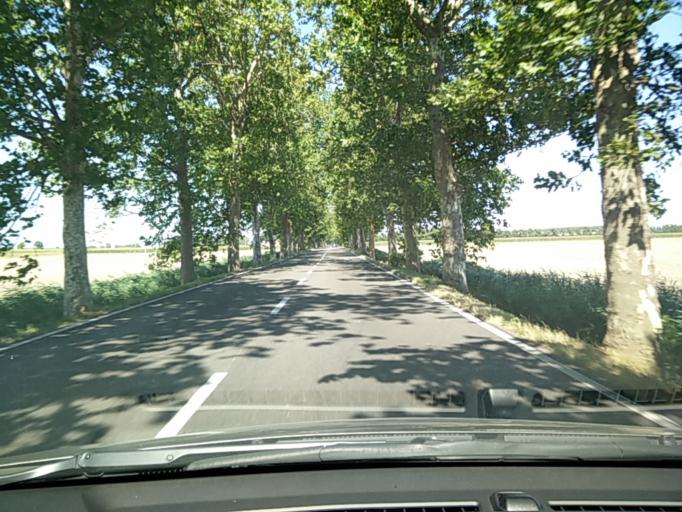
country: IT
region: Veneto
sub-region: Provincia di Venezia
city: La Salute di Livenza
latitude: 45.6740
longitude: 12.8118
